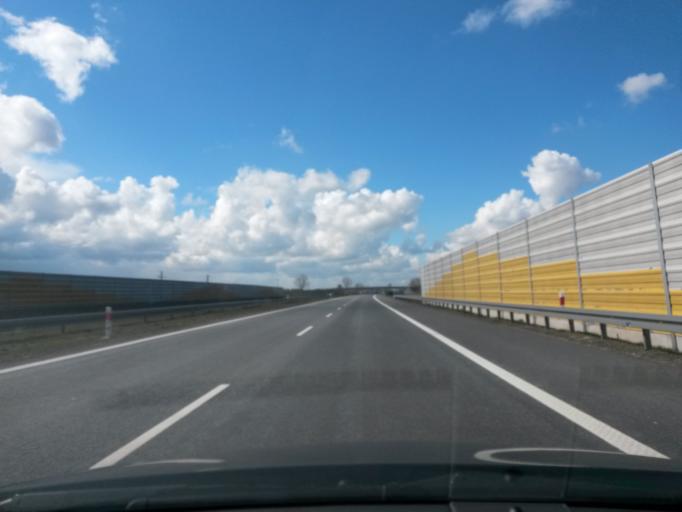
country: PL
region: Lodz Voivodeship
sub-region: Powiat poddebicki
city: Wartkowice
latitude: 52.0022
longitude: 18.9961
